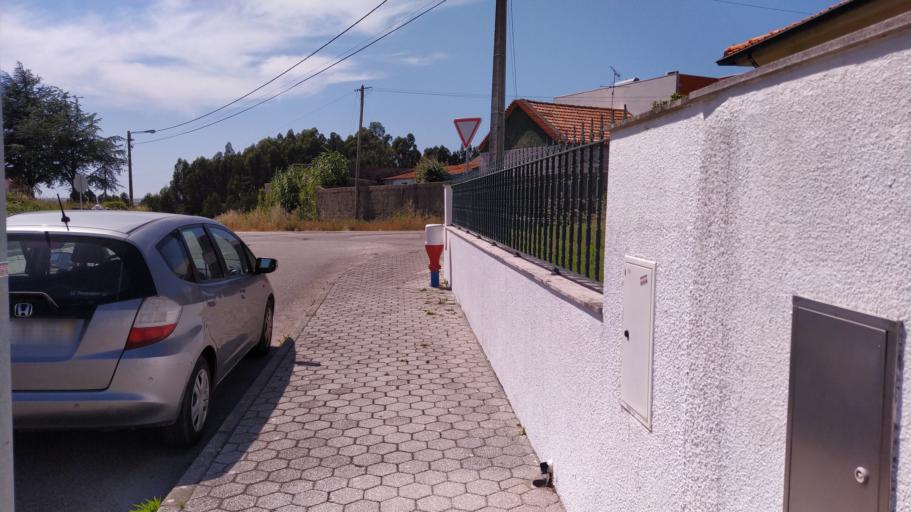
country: PT
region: Aveiro
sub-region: Aveiro
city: Aveiro
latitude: 40.6576
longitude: -8.6337
